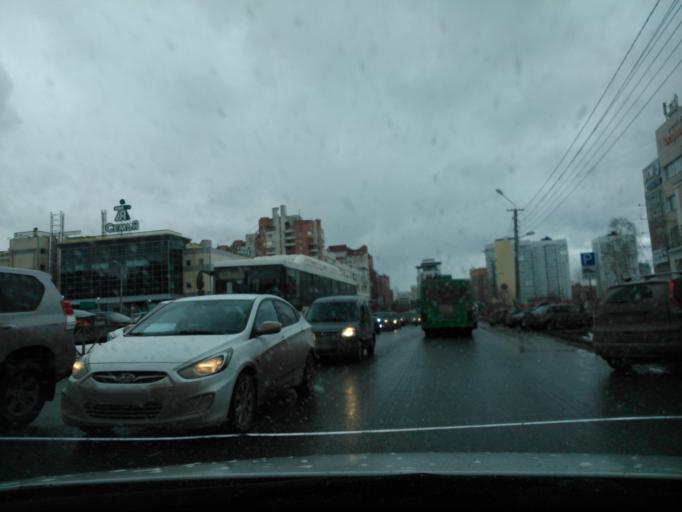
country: RU
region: Perm
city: Perm
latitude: 58.0068
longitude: 56.2649
